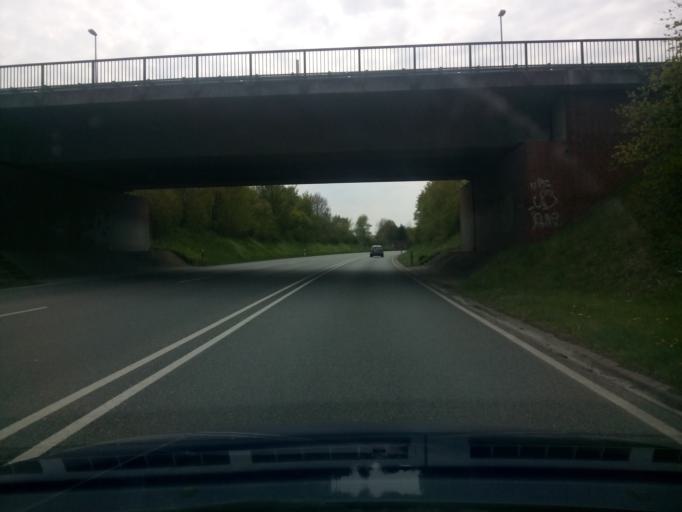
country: DE
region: Lower Saxony
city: Stuhr
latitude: 53.0045
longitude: 8.7979
